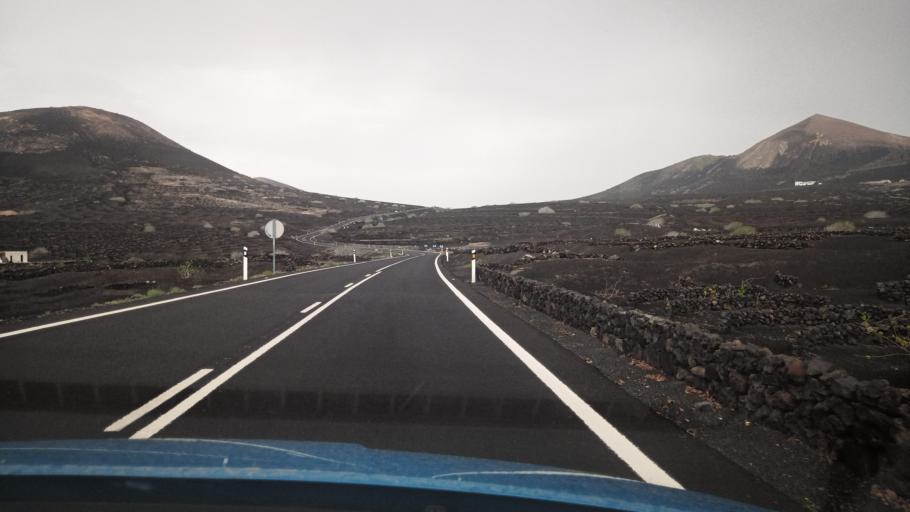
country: ES
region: Canary Islands
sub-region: Provincia de Las Palmas
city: Yaiza
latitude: 28.9600
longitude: -13.7296
